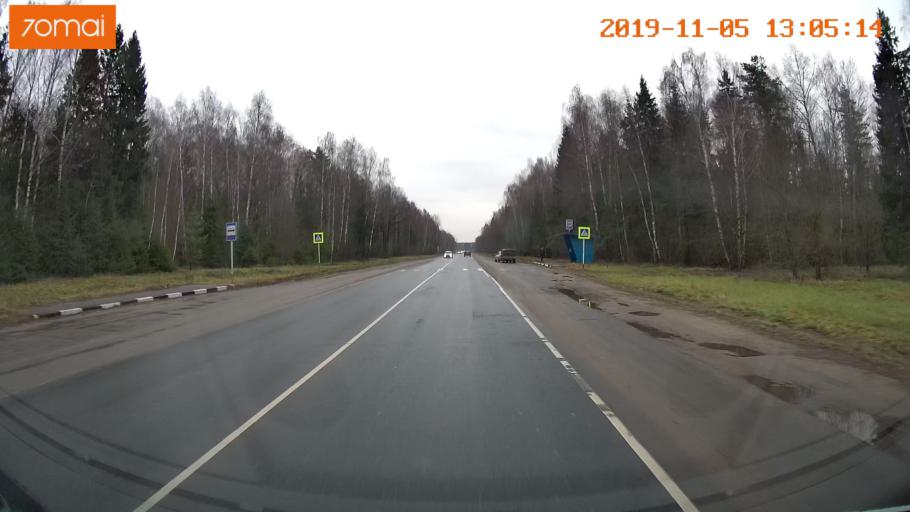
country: RU
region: Ivanovo
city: Kitovo
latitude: 56.8838
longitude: 41.2385
